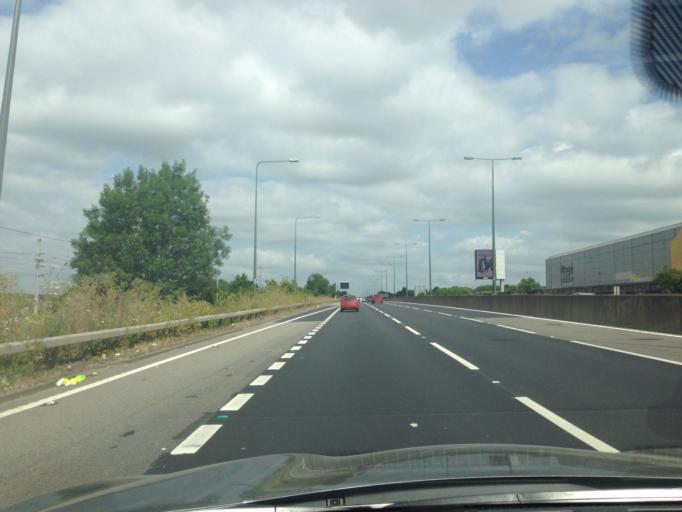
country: GB
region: England
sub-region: Greater London
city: Hendon
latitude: 51.6062
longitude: -0.2420
